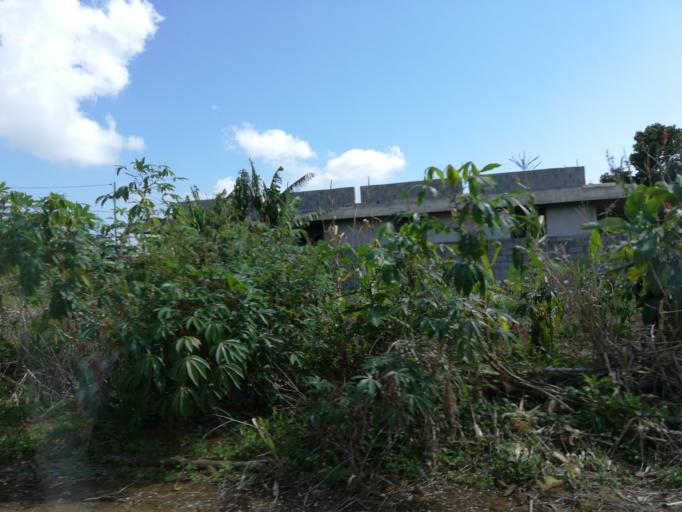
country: MU
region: Moka
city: Verdun
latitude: -20.2267
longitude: 57.5443
